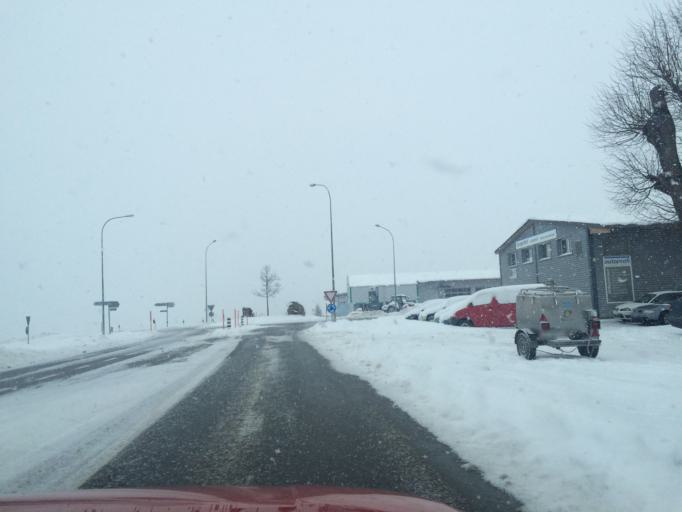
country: CH
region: Bern
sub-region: Bern-Mittelland District
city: Rueggisberg
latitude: 46.8233
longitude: 7.4504
